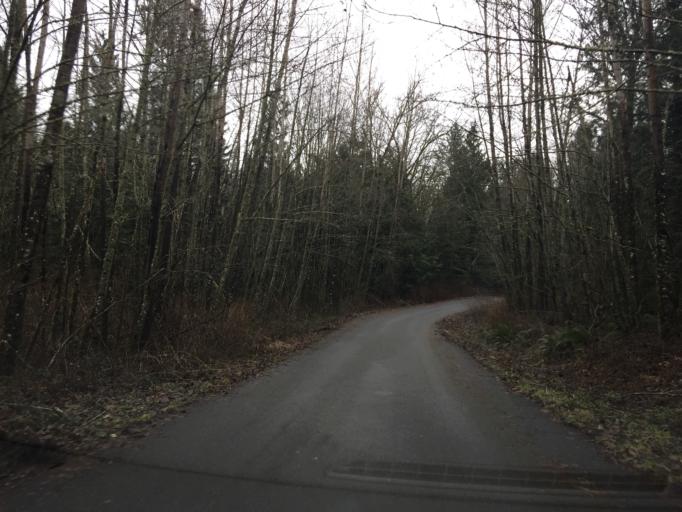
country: US
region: Washington
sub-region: Whatcom County
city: Geneva
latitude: 48.8081
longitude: -122.4317
